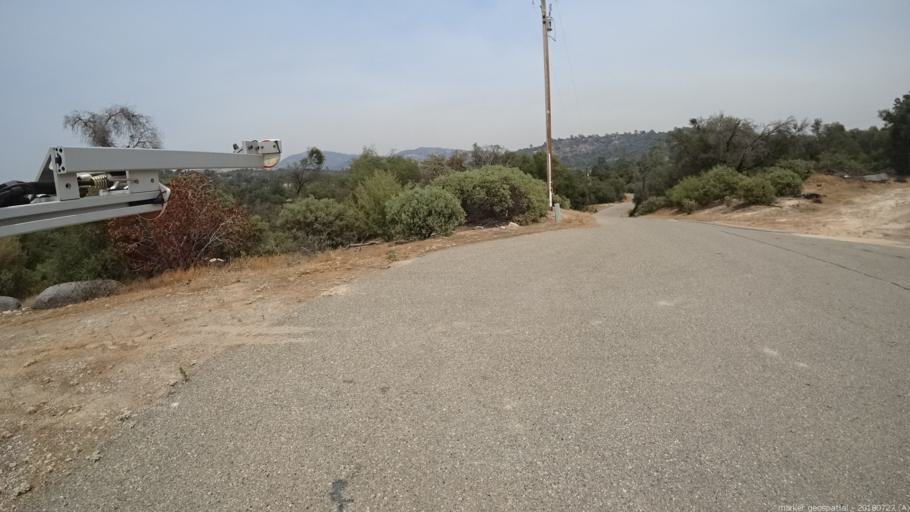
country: US
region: California
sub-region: Madera County
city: Coarsegold
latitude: 37.2479
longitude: -119.7125
